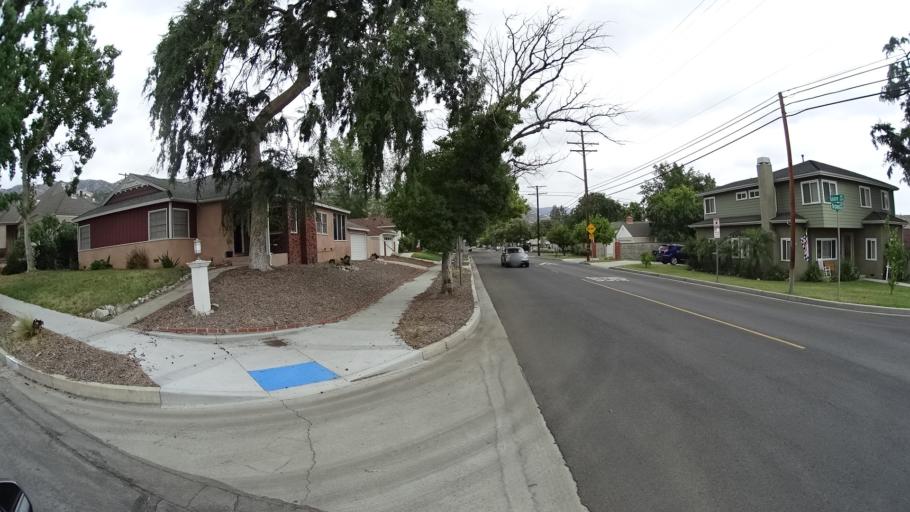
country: US
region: California
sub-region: Los Angeles County
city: Burbank
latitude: 34.2028
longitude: -118.3303
